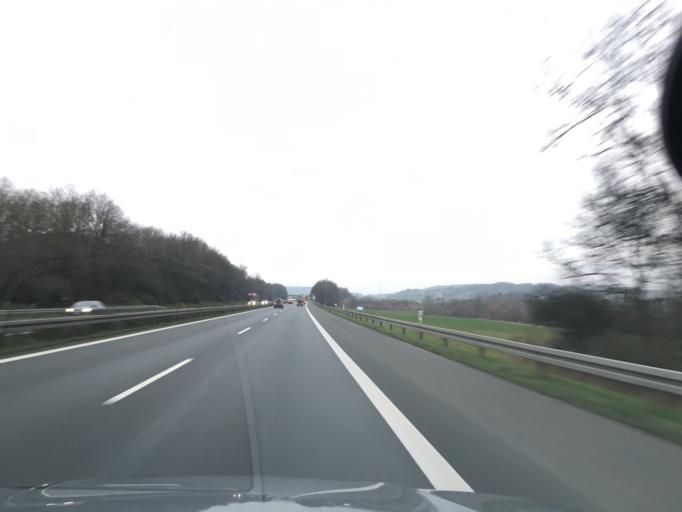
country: DE
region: Bavaria
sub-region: Regierungsbezirk Unterfranken
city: Geiselwind
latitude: 49.7655
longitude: 10.5111
